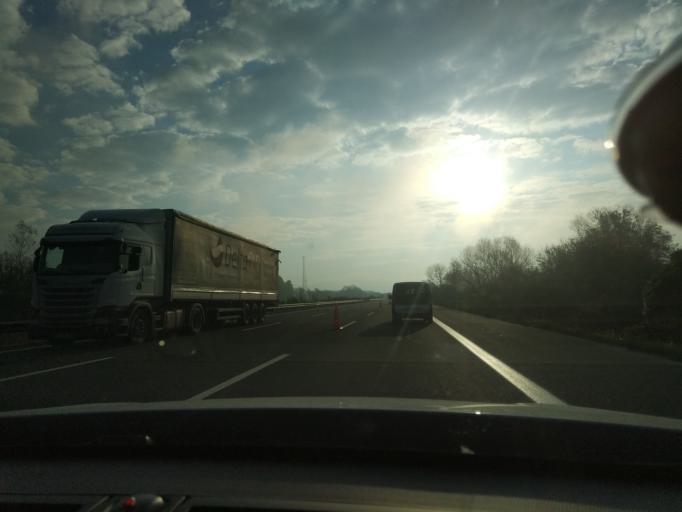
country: TR
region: Duzce
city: Duzce
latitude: 40.8125
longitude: 31.1076
